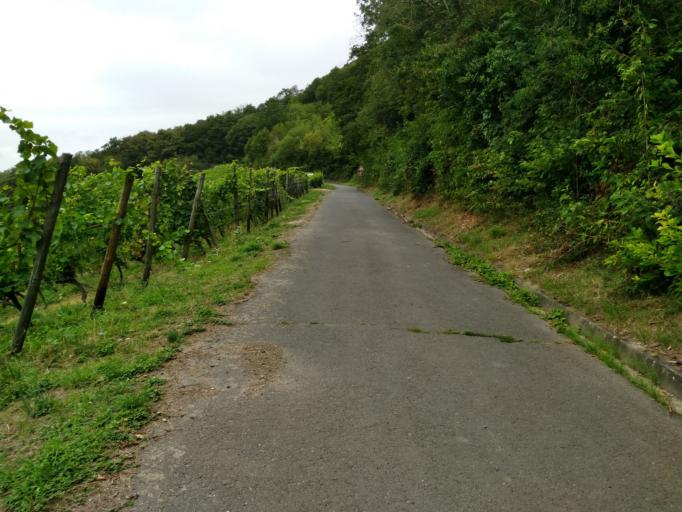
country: DE
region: North Rhine-Westphalia
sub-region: Regierungsbezirk Koln
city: Konigswinter
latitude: 50.6647
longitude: 7.2055
